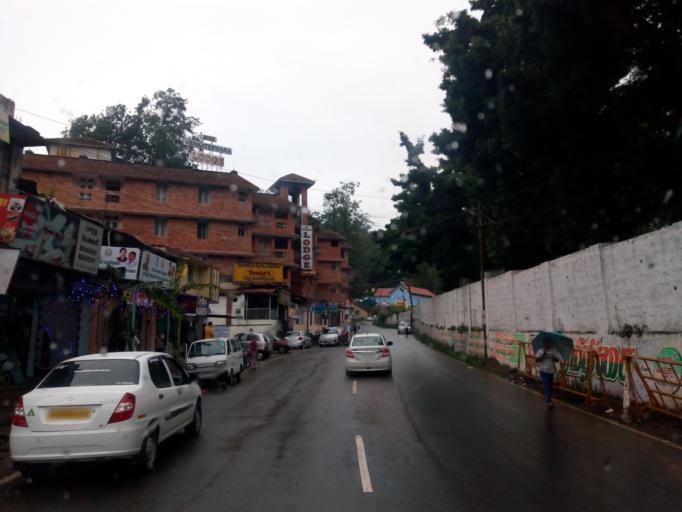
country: IN
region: Tamil Nadu
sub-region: Nilgiri
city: Wellington
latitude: 11.3436
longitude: 76.7929
